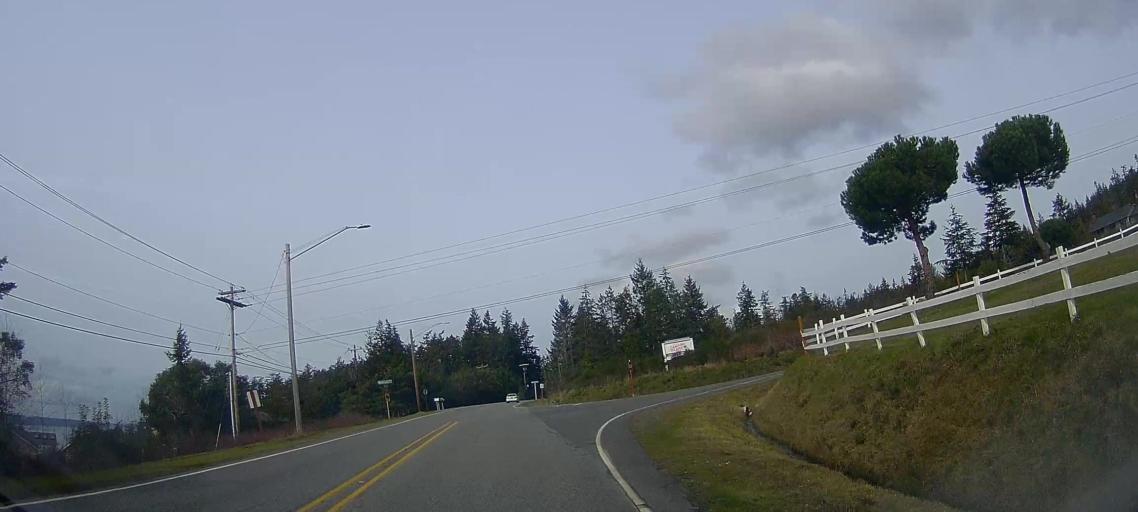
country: US
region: Washington
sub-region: Island County
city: Camano
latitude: 48.1564
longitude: -122.5161
